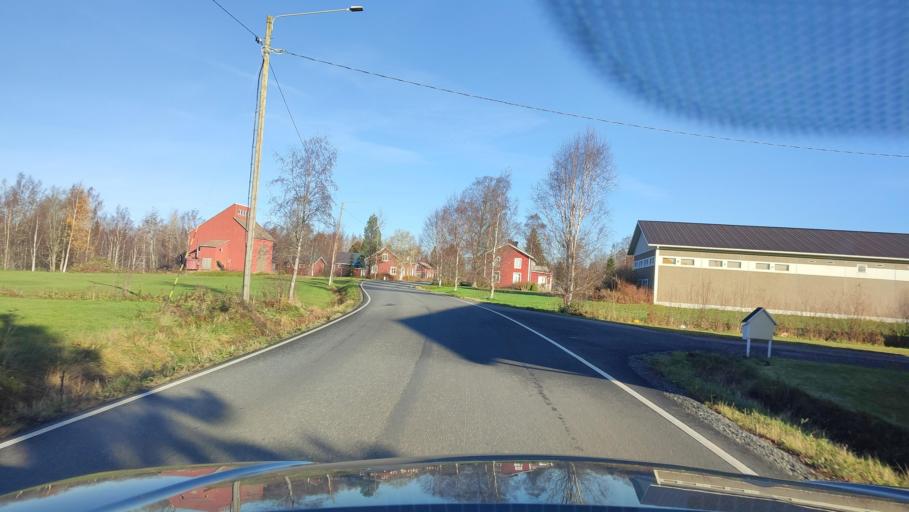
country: FI
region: Southern Ostrobothnia
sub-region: Suupohja
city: Karijoki
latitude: 62.2766
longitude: 21.7078
